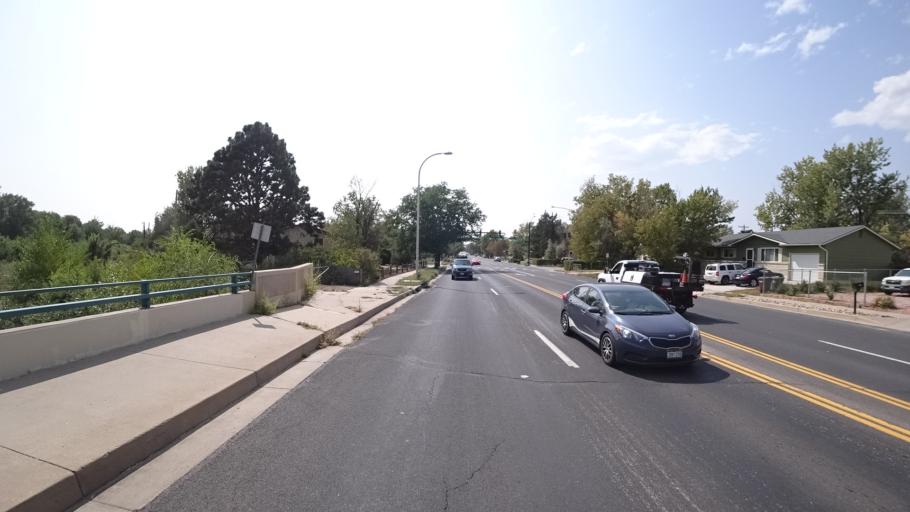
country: US
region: Colorado
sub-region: El Paso County
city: Cimarron Hills
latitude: 38.8513
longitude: -104.7478
